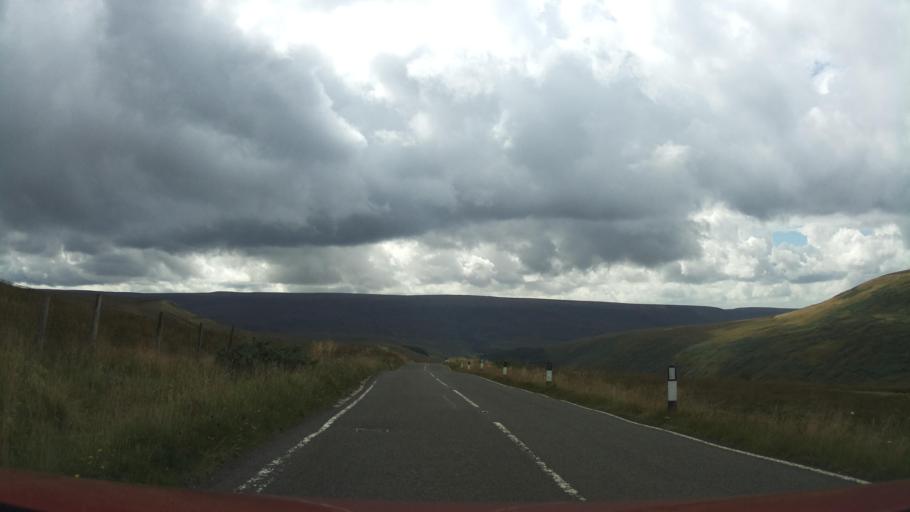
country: GB
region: England
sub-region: Kirklees
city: Meltham
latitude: 53.5224
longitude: -1.8515
